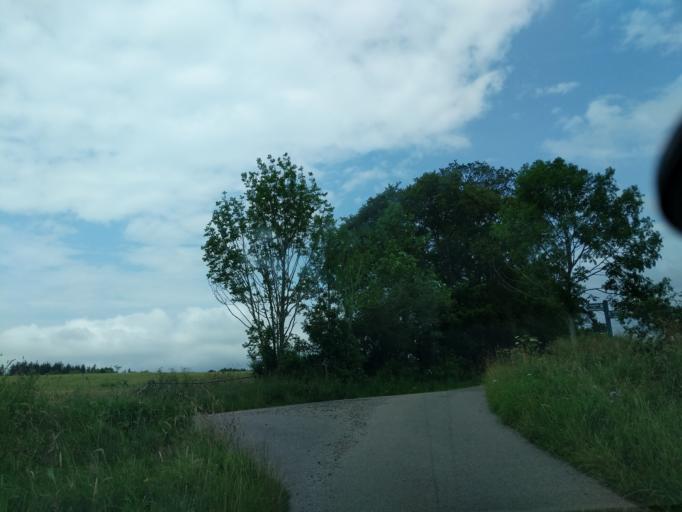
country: GB
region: Scotland
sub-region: Moray
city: Rothes
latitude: 57.4726
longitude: -3.2367
